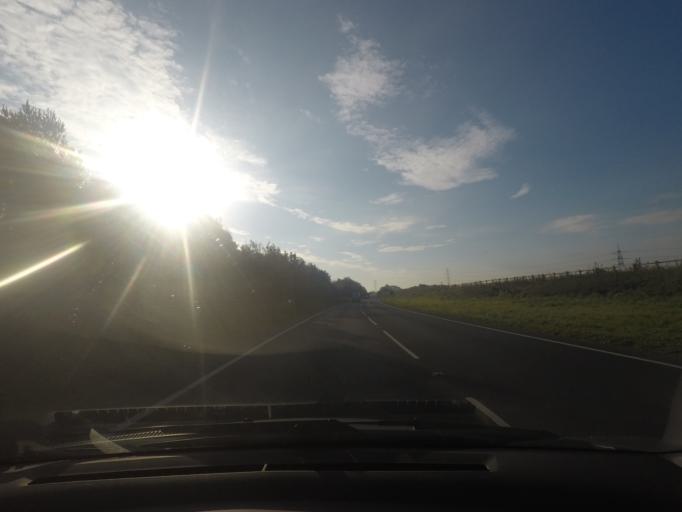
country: GB
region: England
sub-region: East Riding of Yorkshire
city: Londesborough
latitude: 53.8676
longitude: -0.6842
